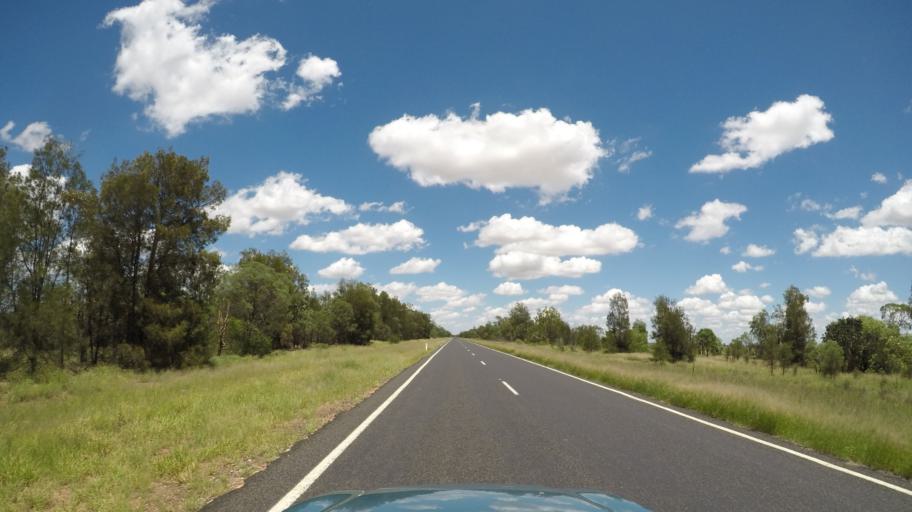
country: AU
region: Queensland
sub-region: Goondiwindi
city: Goondiwindi
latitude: -28.1679
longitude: 150.5948
